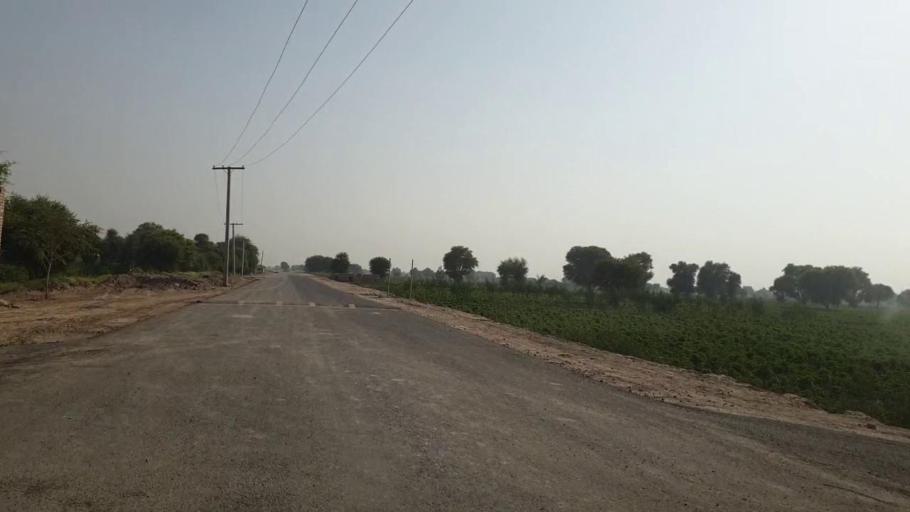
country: PK
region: Sindh
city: Bhan
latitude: 26.5335
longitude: 67.7885
